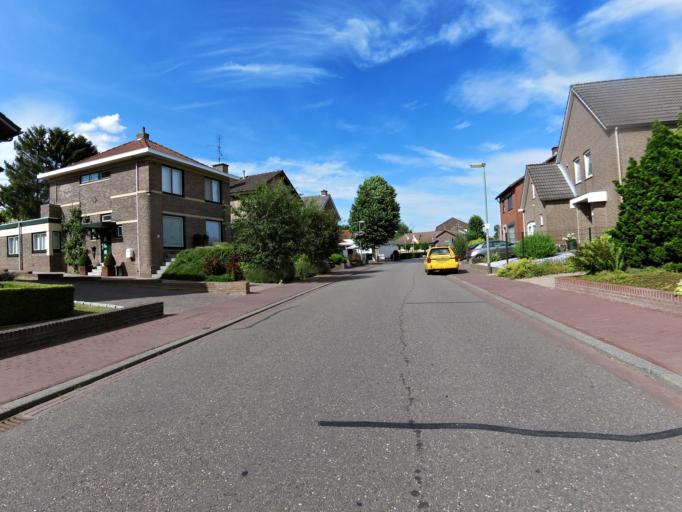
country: NL
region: Limburg
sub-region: Gemeente Schinnen
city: Doenrade
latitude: 50.9673
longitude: 5.9058
